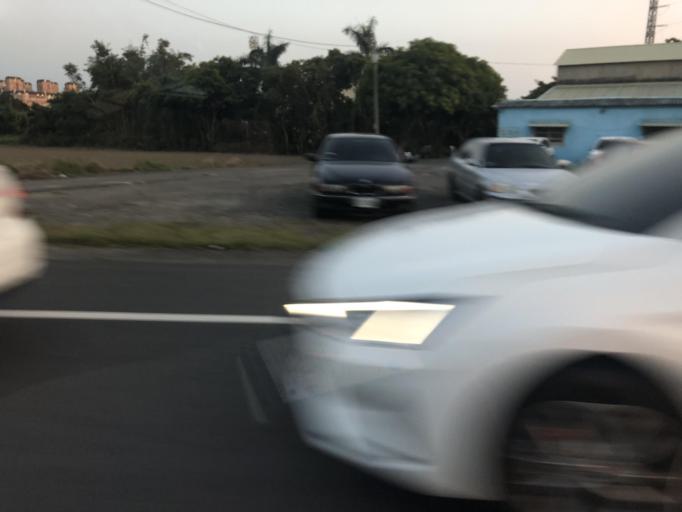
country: TW
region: Taiwan
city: Xinying
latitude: 23.2999
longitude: 120.2914
